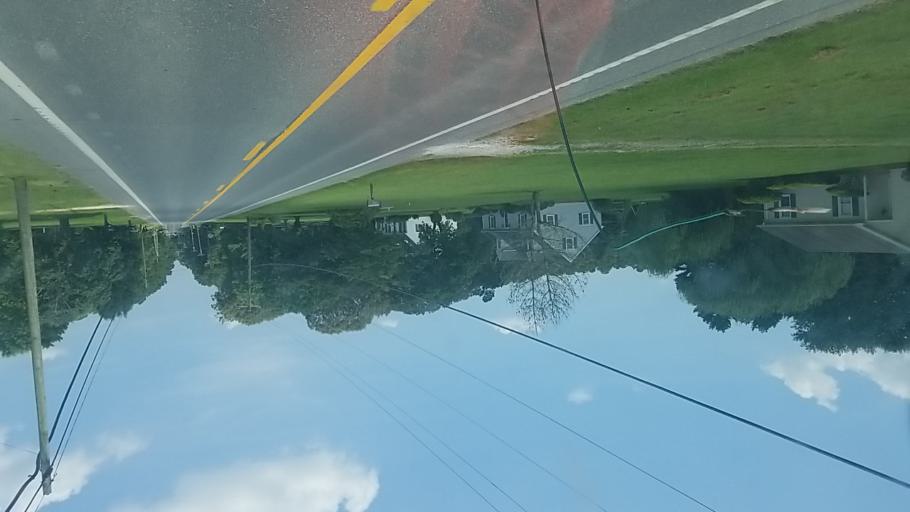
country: US
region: Maryland
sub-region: Wicomico County
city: Salisbury
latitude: 38.3544
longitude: -75.5299
